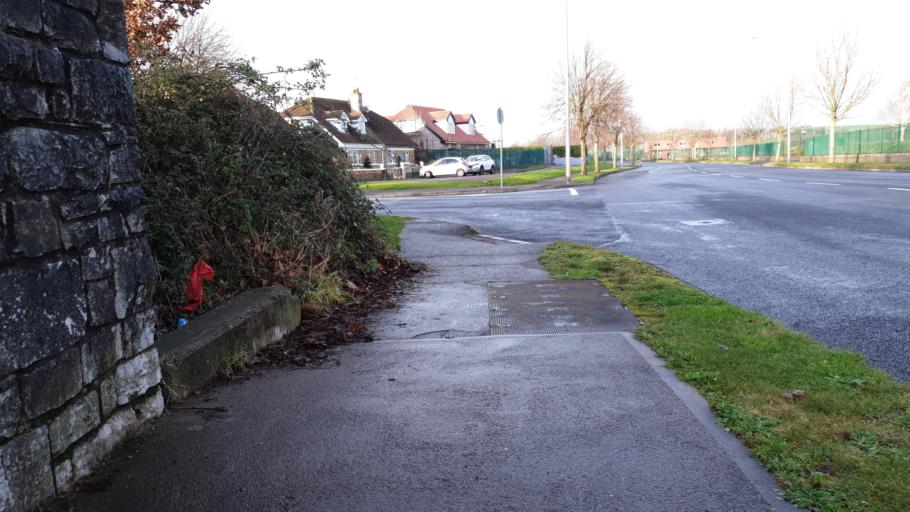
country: IE
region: Munster
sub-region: County Cork
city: Passage West
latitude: 51.8902
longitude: -8.3951
